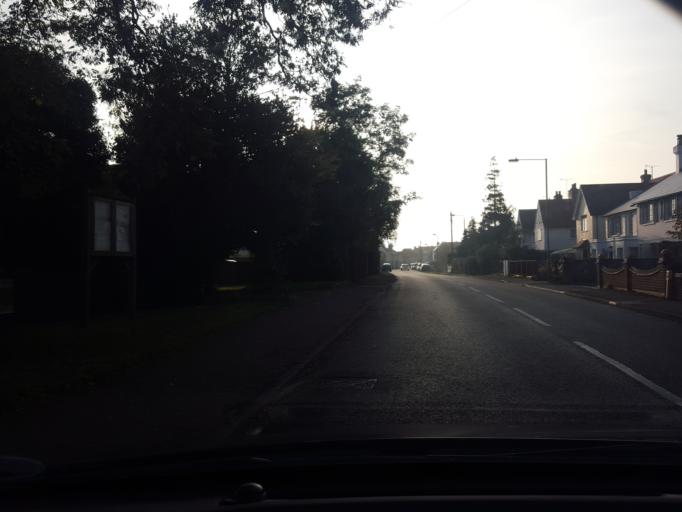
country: GB
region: England
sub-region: Essex
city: Saint Osyth
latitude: 51.8005
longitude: 1.0824
